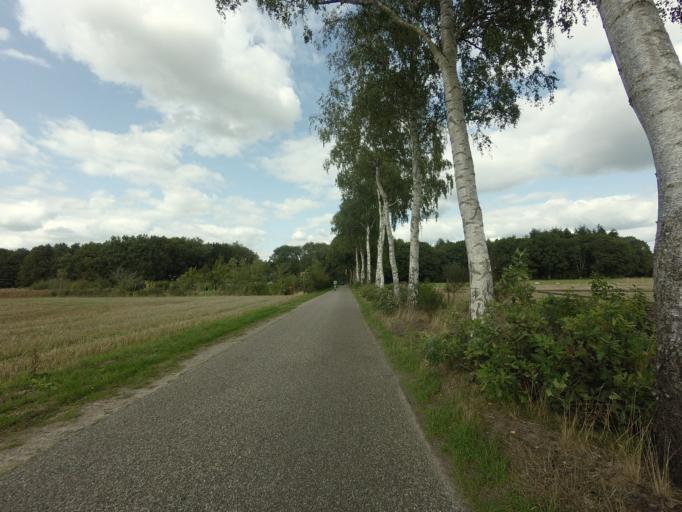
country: NL
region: Drenthe
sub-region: Gemeente De Wolden
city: Ruinen
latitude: 52.7800
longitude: 6.3666
